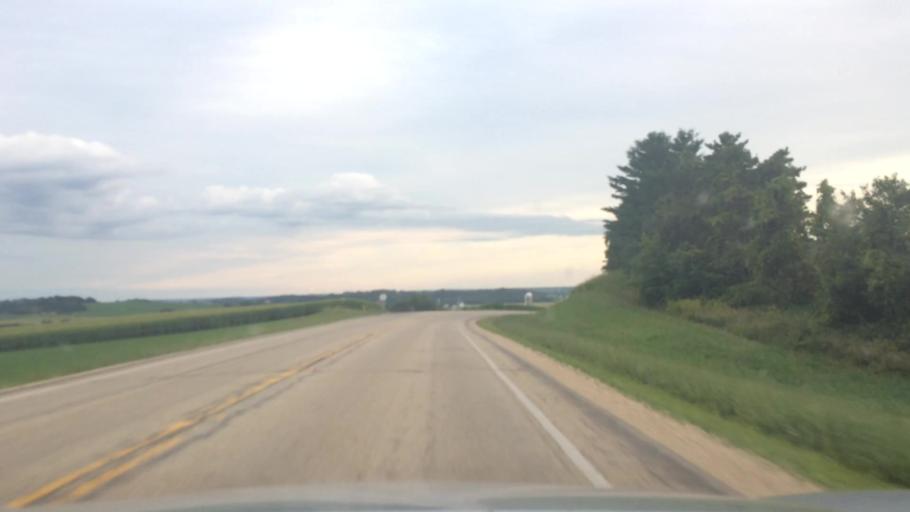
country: US
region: Wisconsin
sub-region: Columbia County
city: Lodi
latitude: 43.2396
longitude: -89.5211
